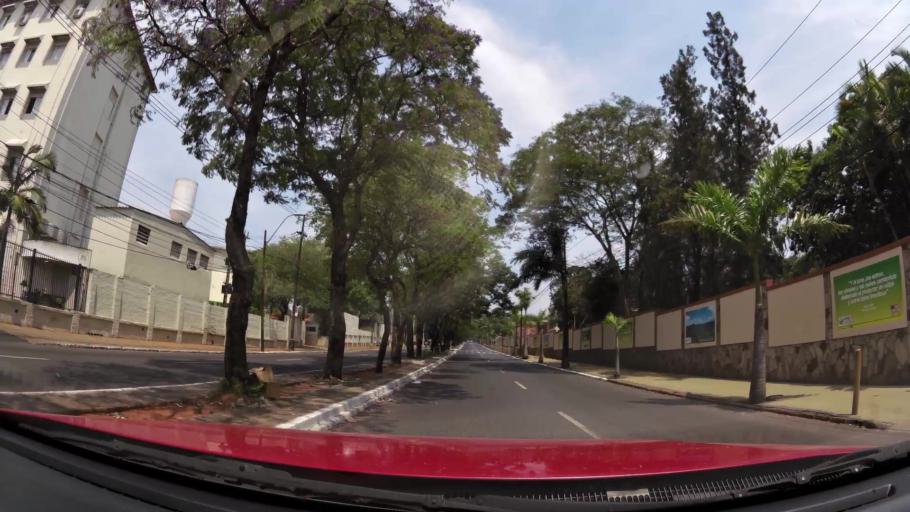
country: PY
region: Asuncion
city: Asuncion
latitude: -25.2927
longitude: -57.6033
